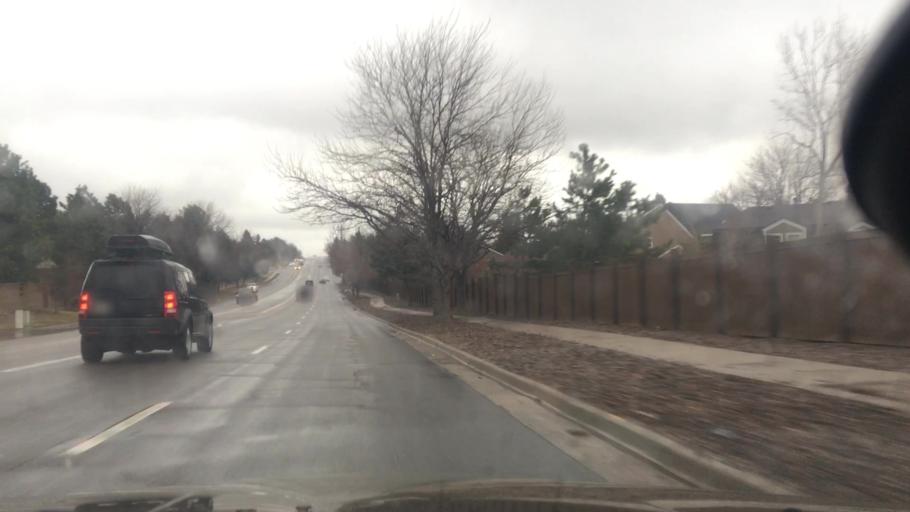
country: US
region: Colorado
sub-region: Arapahoe County
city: Castlewood
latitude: 39.5740
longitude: -104.9229
